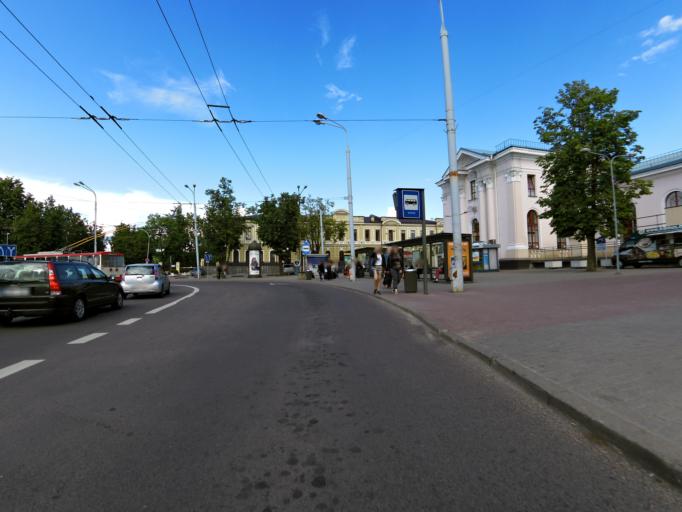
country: LT
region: Vilnius County
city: Naujamiestis
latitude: 54.6706
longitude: 25.2845
